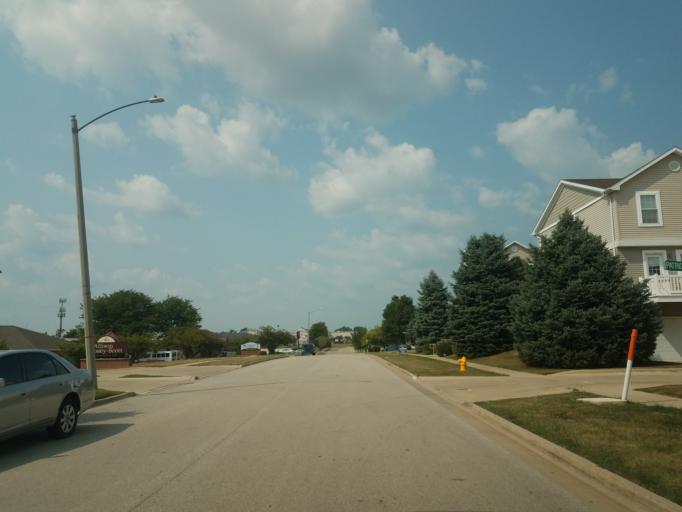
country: US
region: Illinois
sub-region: McLean County
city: Bloomington
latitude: 40.4824
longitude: -88.9463
